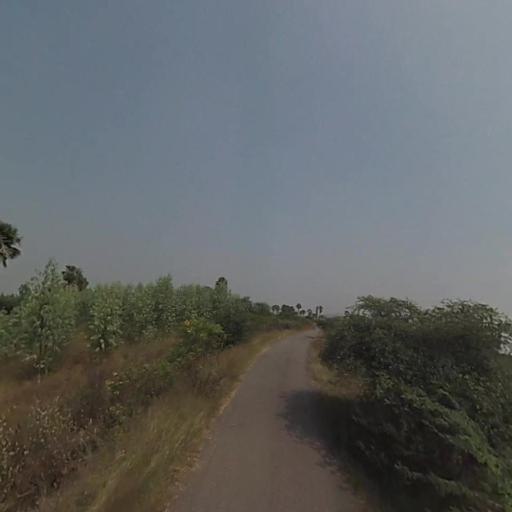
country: IN
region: Telangana
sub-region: Nalgonda
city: Nalgonda
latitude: 17.1994
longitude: 79.1421
